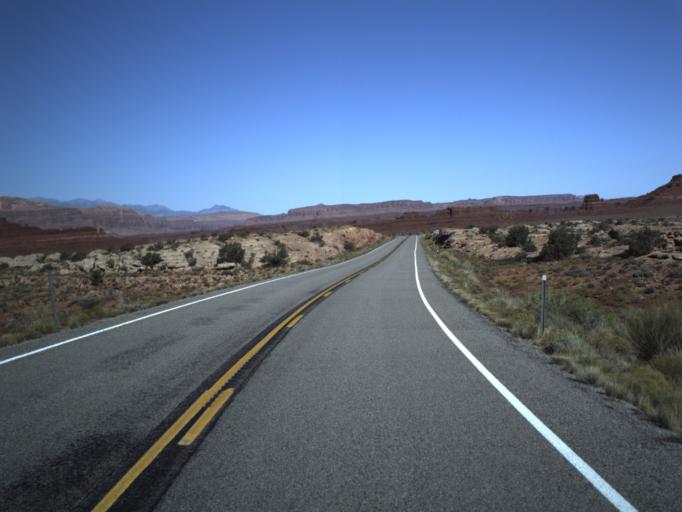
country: US
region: Utah
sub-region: San Juan County
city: Blanding
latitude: 37.8128
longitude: -110.3423
